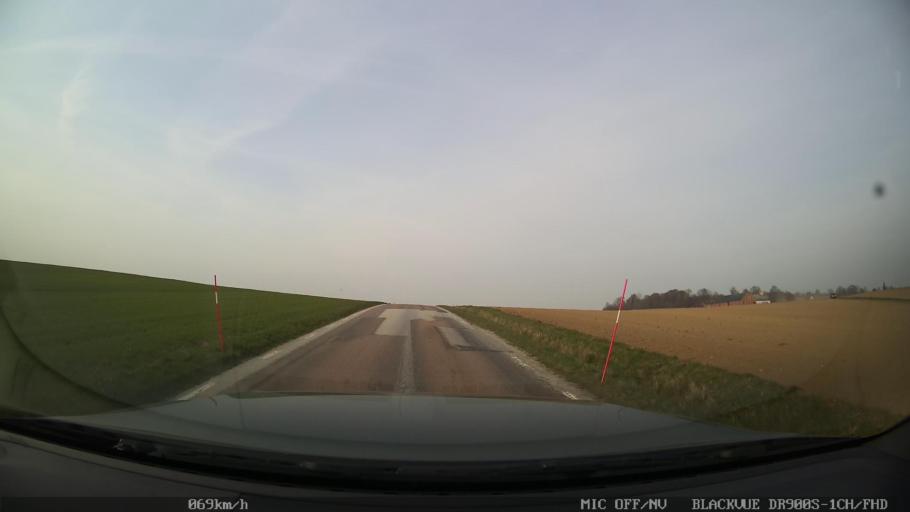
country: SE
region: Skane
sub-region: Ystads Kommun
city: Ystad
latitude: 55.4490
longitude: 13.8317
